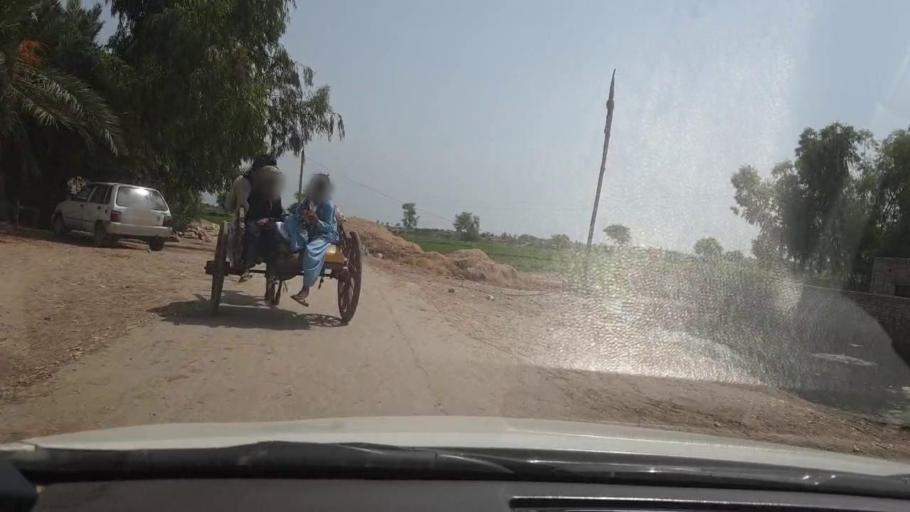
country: PK
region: Sindh
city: Shikarpur
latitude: 27.9425
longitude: 68.5977
